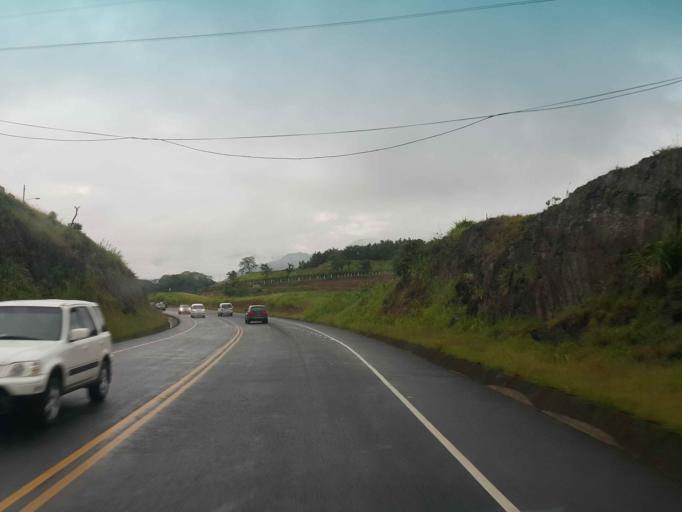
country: CR
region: Heredia
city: Colon
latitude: 9.9435
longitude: -84.2291
